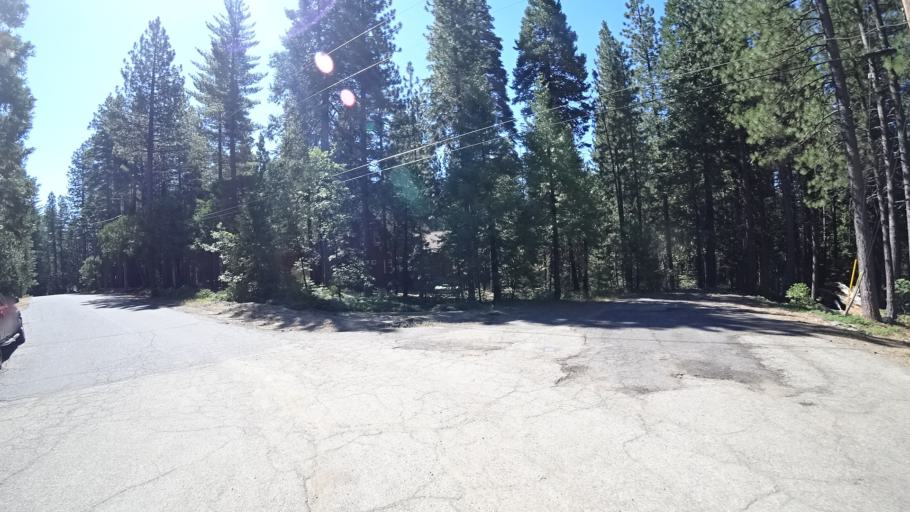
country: US
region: California
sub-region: Calaveras County
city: Arnold
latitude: 38.2800
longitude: -120.2831
